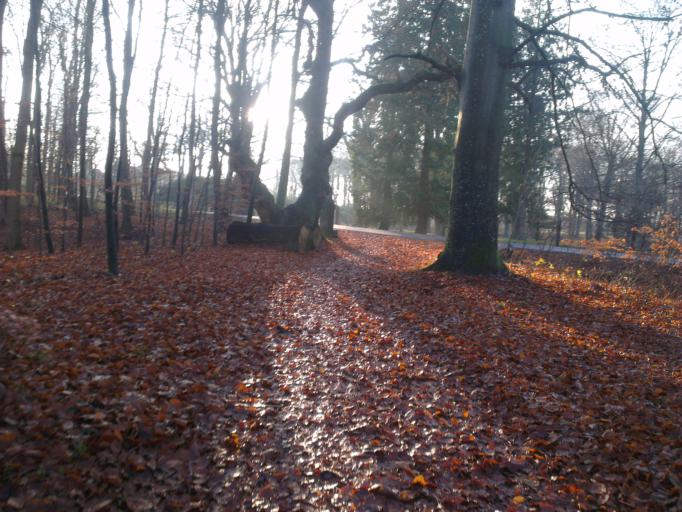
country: DK
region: Capital Region
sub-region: Frederikssund Kommune
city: Jaegerspris
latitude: 55.8576
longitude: 11.9828
